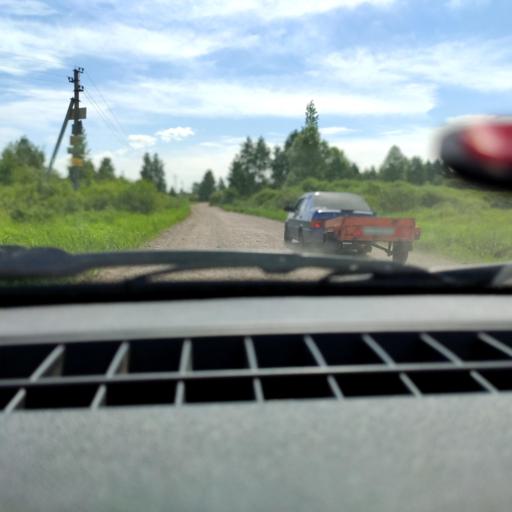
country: RU
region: Bashkortostan
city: Kabakovo
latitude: 54.7326
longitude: 56.2003
